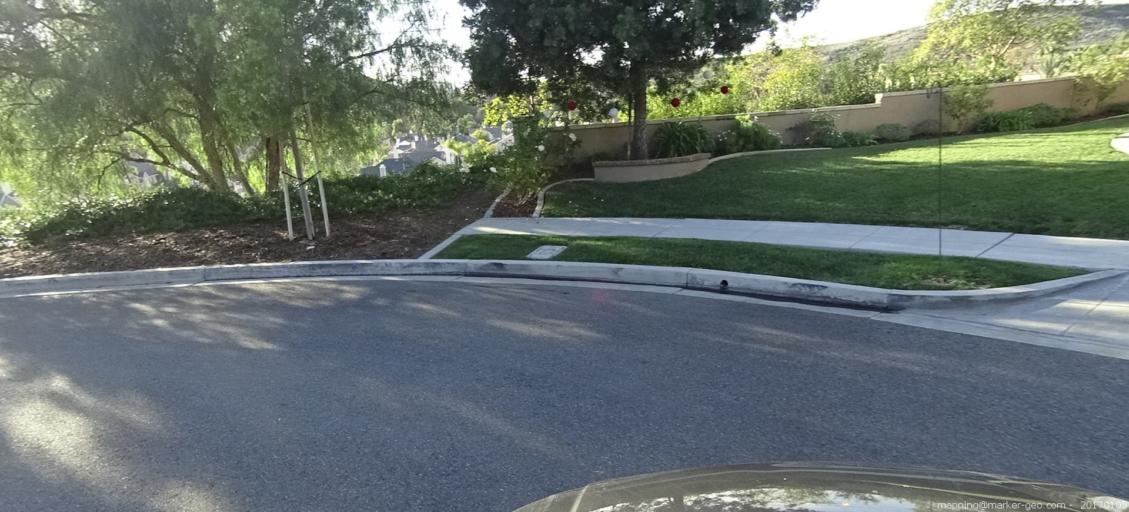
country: US
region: California
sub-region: Orange County
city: Ladera Ranch
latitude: 33.5539
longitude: -117.6422
